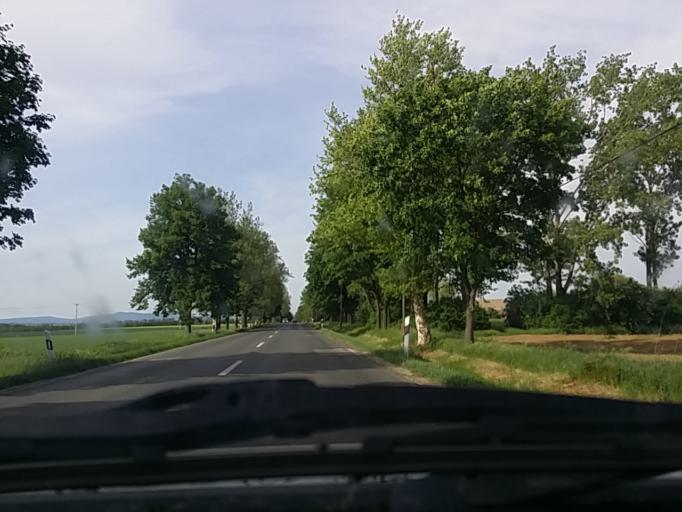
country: HU
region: Baranya
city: Harkany
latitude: 45.9195
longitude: 18.2331
